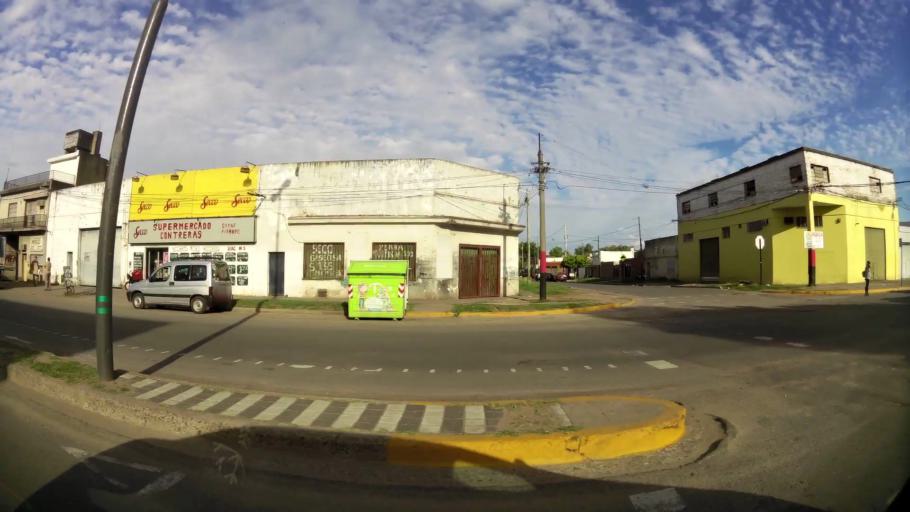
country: AR
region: Santa Fe
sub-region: Departamento de Rosario
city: Rosario
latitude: -32.9805
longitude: -60.6714
